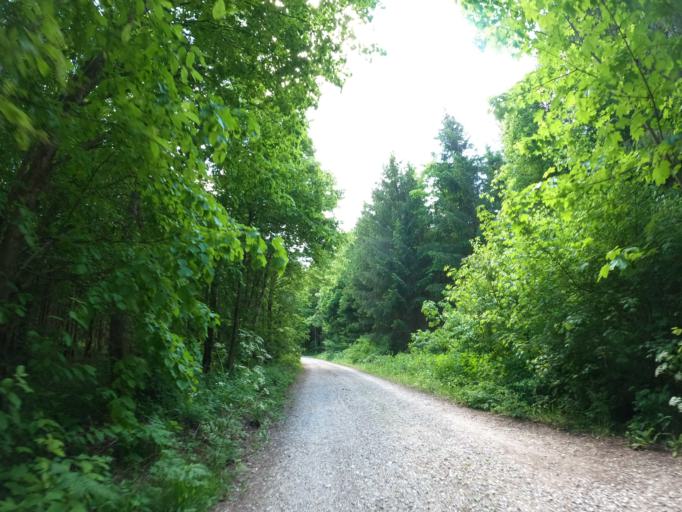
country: DE
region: Bavaria
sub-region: Upper Bavaria
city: Oberhaching
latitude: 48.0208
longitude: 11.6232
